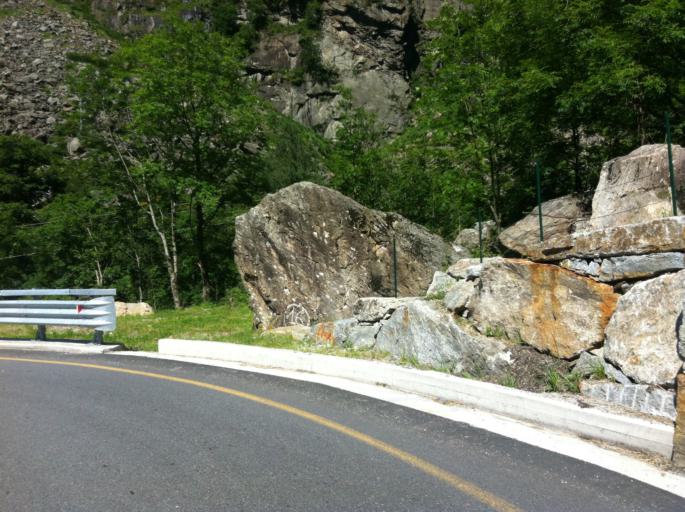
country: IT
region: Lombardy
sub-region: Provincia di Sondrio
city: Campodolcino
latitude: 46.4091
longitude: 9.3510
